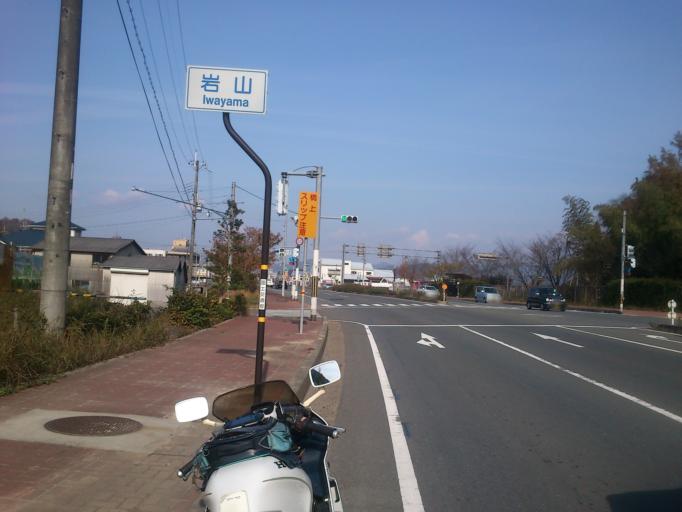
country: JP
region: Kyoto
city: Kameoka
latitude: 35.1496
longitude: 135.4285
